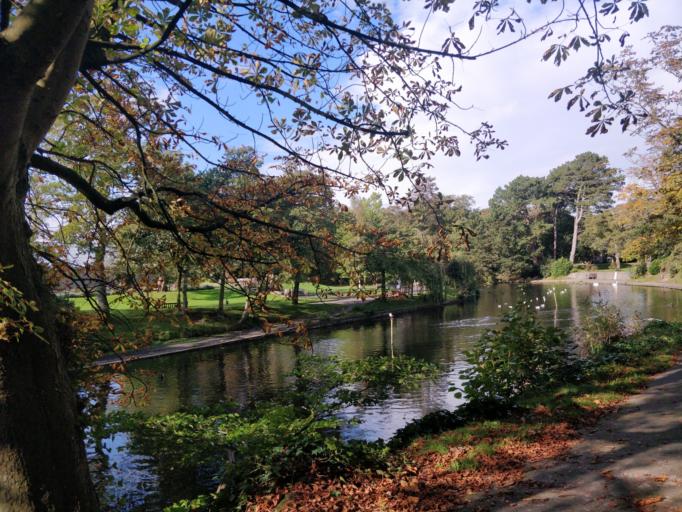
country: GB
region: England
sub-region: Lancashire
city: Banks
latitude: 53.6607
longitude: -2.9587
